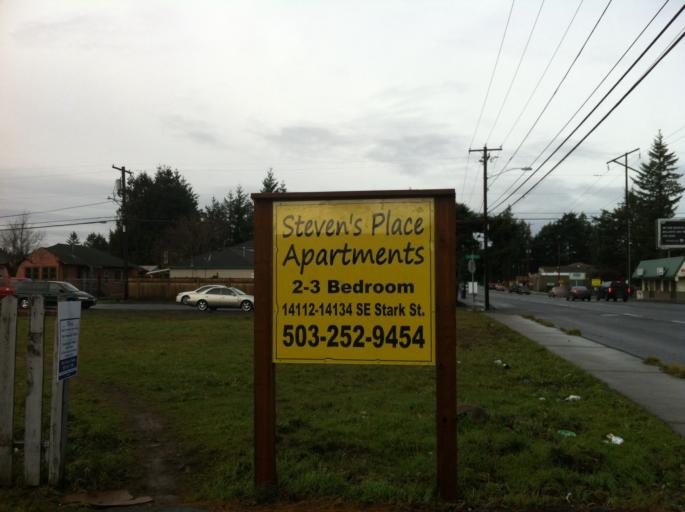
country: US
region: Oregon
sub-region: Multnomah County
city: Lents
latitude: 45.5190
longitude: -122.5179
